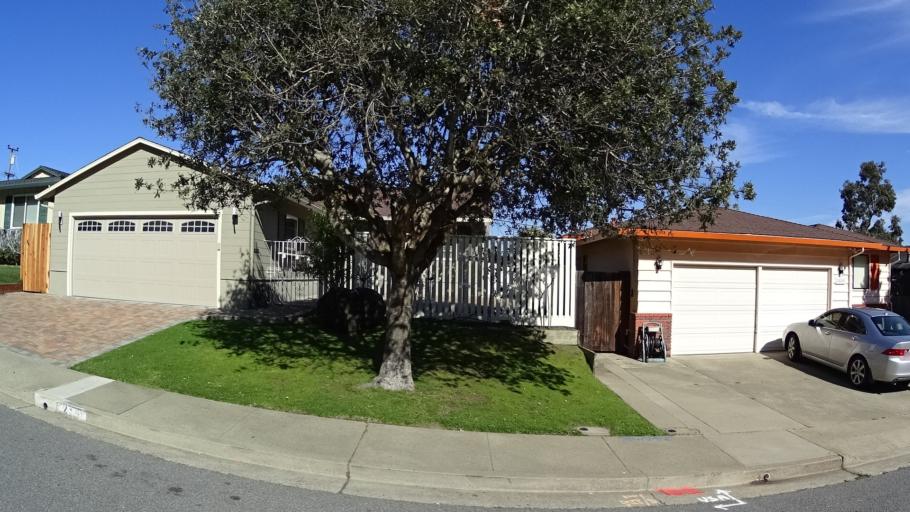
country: US
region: California
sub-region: San Mateo County
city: Pacifica
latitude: 37.6386
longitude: -122.4591
